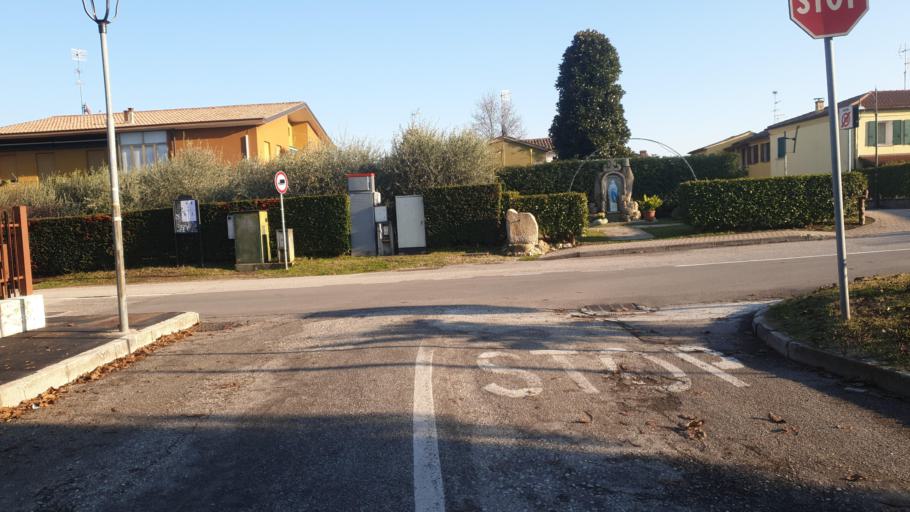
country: IT
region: Veneto
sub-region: Provincia di Padova
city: Galzignano
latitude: 45.3057
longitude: 11.7405
